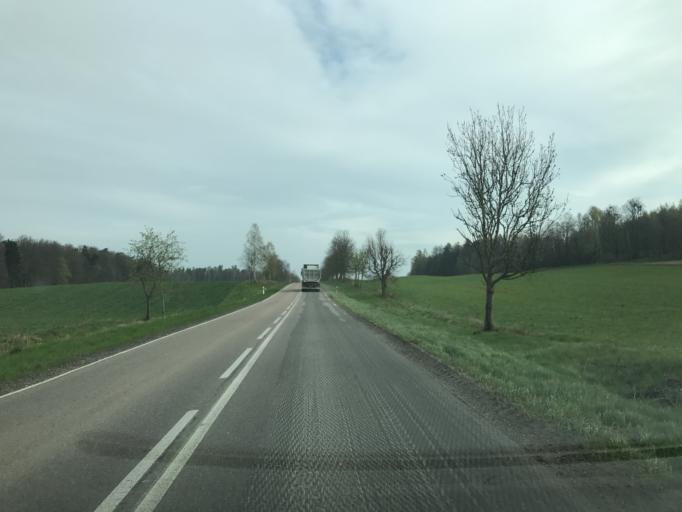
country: PL
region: Warmian-Masurian Voivodeship
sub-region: Powiat ostrodzki
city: Gierzwald
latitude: 53.5508
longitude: 20.0898
